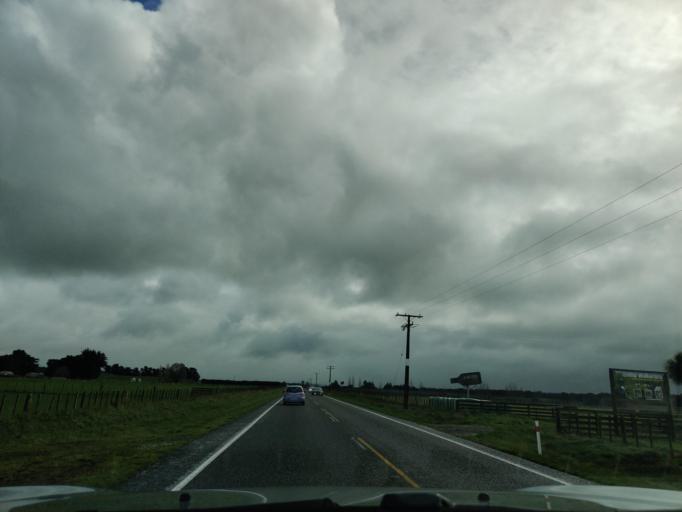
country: NZ
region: Hawke's Bay
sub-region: Hastings District
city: Hastings
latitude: -40.0208
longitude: 176.3160
